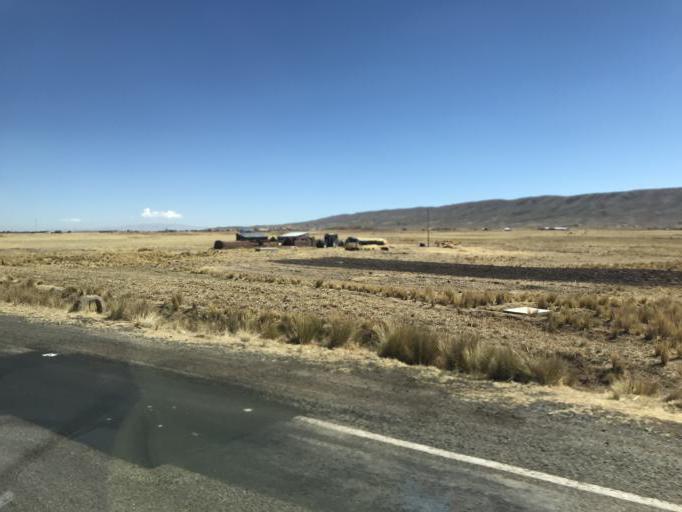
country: BO
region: La Paz
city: Tiahuanaco
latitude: -16.5688
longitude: -68.6595
